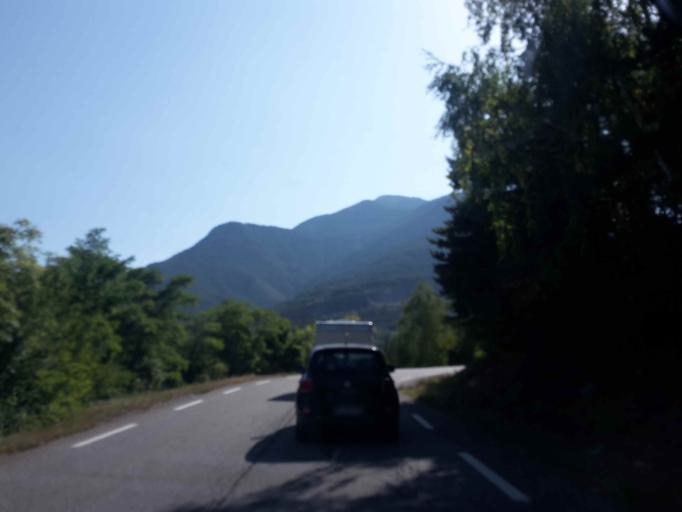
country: FR
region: Provence-Alpes-Cote d'Azur
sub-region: Departement des Hautes-Alpes
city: Guillestre
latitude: 44.6542
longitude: 6.6509
